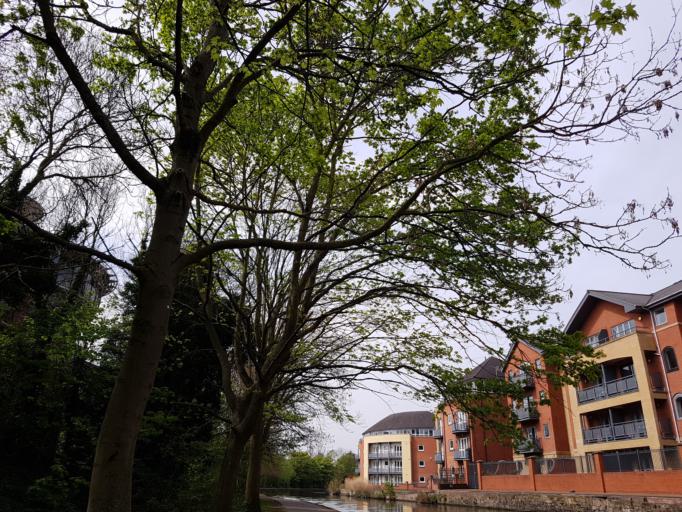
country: GB
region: England
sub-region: Nottingham
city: Nottingham
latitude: 52.9478
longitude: -1.1541
